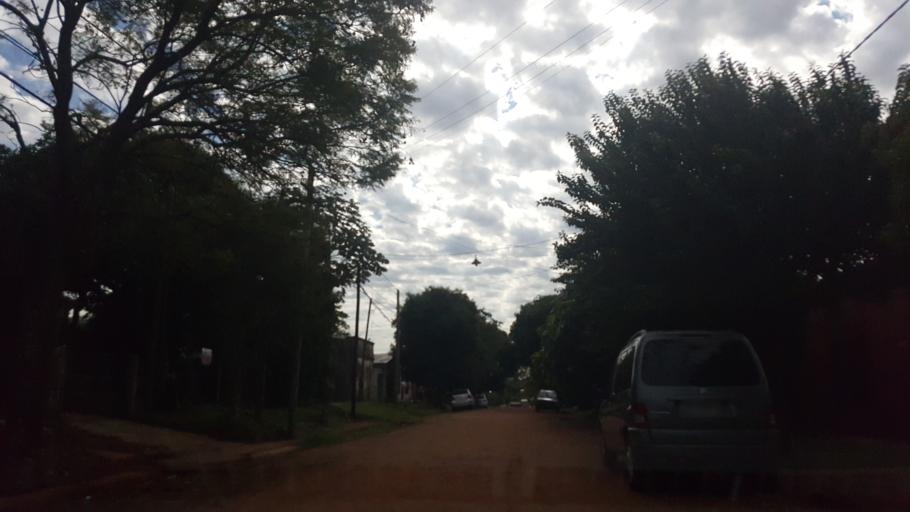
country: AR
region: Misiones
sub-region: Departamento de Capital
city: Posadas
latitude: -27.3706
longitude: -55.9186
